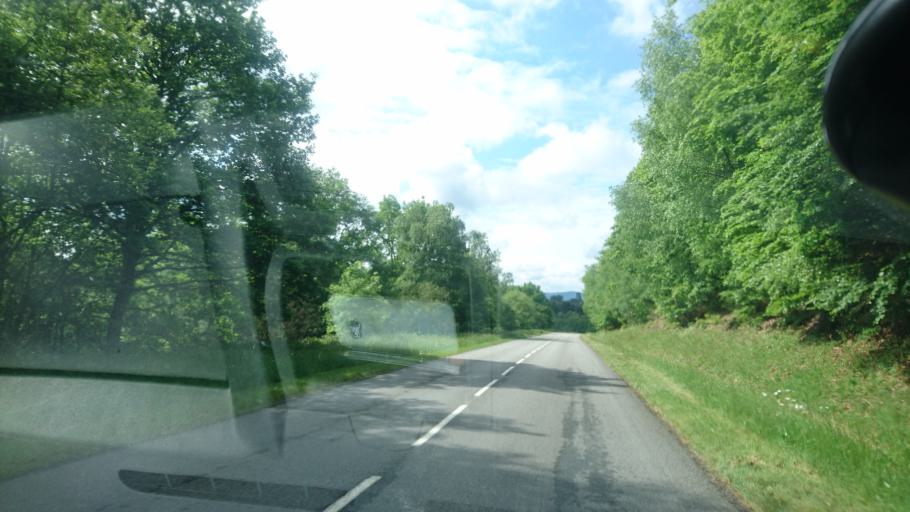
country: FR
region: Limousin
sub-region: Departement de la Haute-Vienne
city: Peyrat-le-Chateau
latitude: 45.7856
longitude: 1.8489
